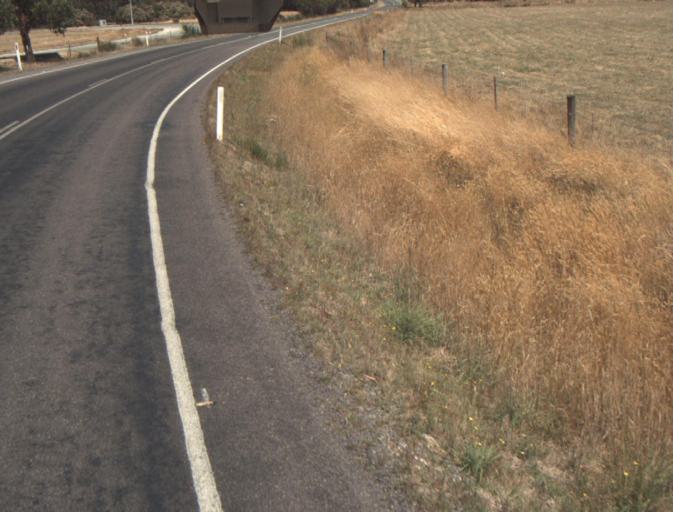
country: AU
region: Tasmania
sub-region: Launceston
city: Newstead
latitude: -41.3297
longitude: 147.3534
